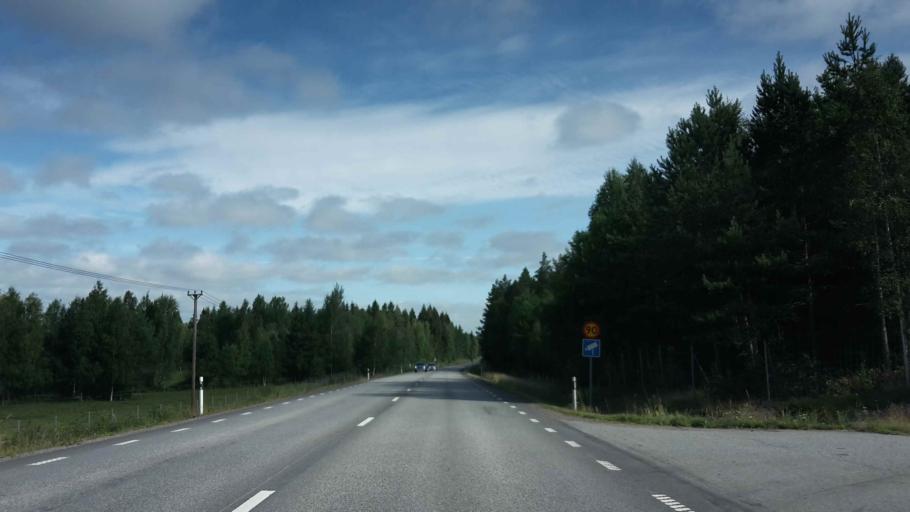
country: SE
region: OErebro
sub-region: Askersunds Kommun
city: Asbro
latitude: 58.9569
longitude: 15.0336
